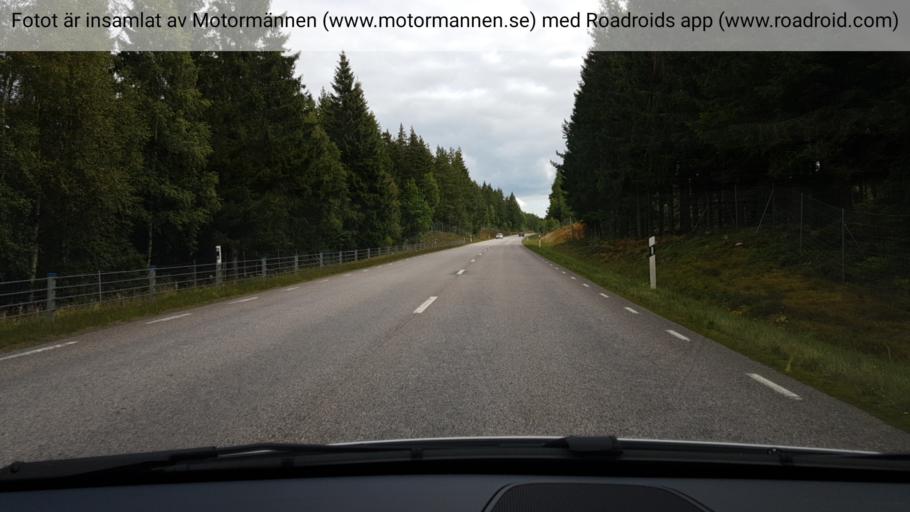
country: SE
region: Vaestra Goetaland
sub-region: Falkopings Kommun
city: Floby
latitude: 58.2058
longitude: 13.2931
